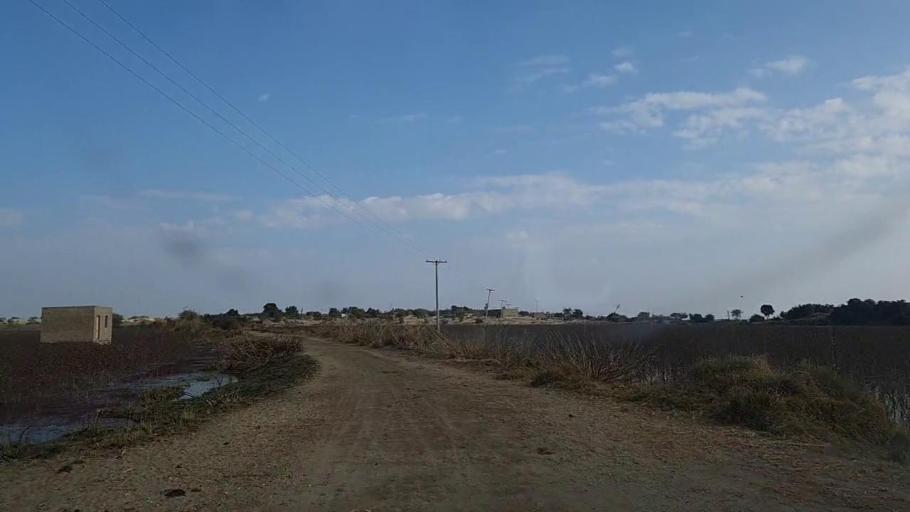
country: PK
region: Sindh
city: Sanghar
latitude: 26.2039
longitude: 69.0229
